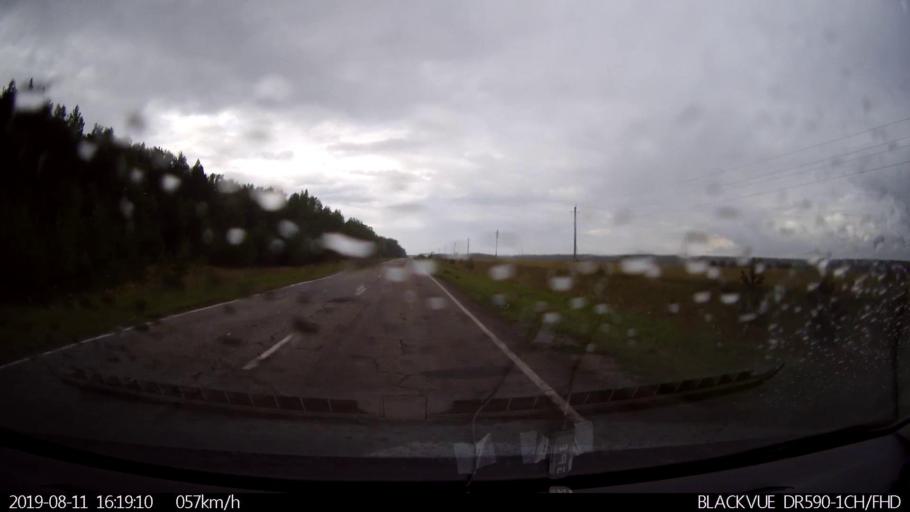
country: RU
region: Ulyanovsk
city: Mayna
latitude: 54.0615
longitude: 47.6087
